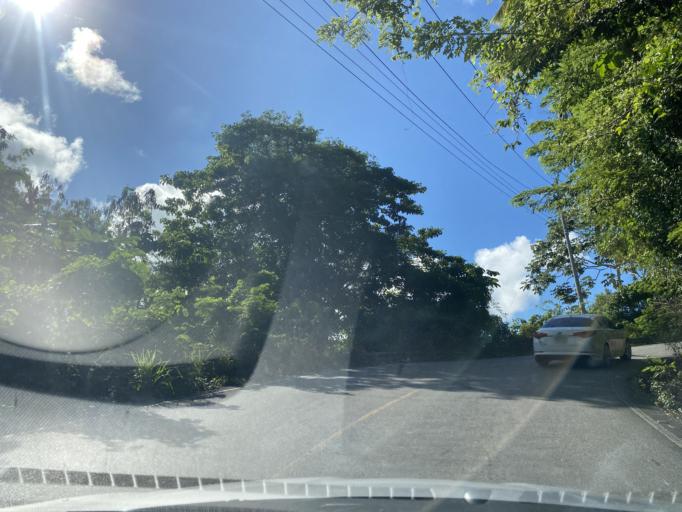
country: DO
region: Samana
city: Sanchez
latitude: 19.2372
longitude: -69.5970
